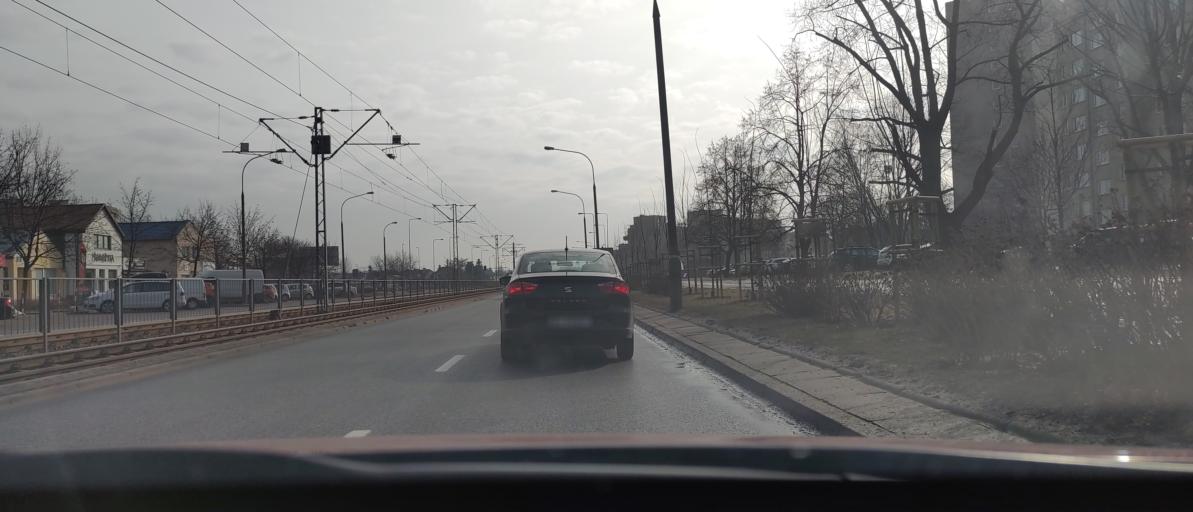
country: PL
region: Masovian Voivodeship
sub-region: Warszawa
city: Bemowo
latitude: 52.2500
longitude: 20.9180
